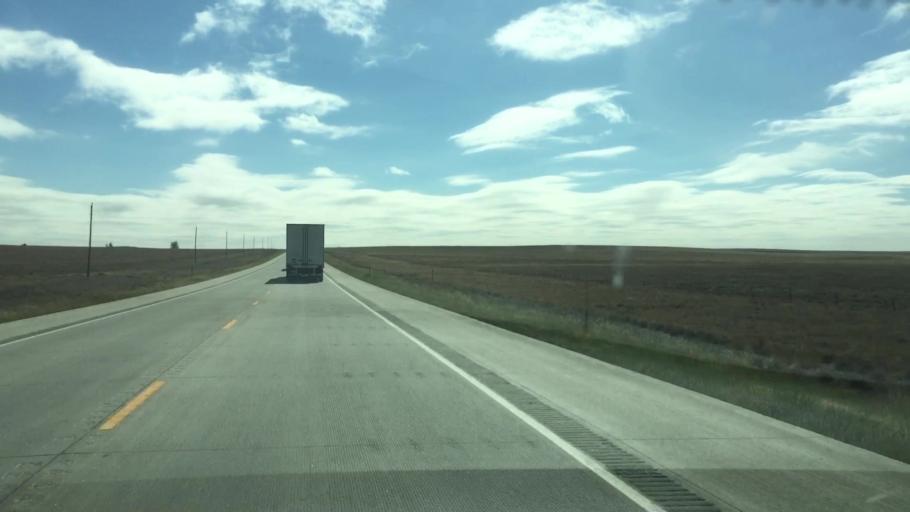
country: US
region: Colorado
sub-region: Lincoln County
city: Hugo
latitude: 39.0412
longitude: -103.3376
